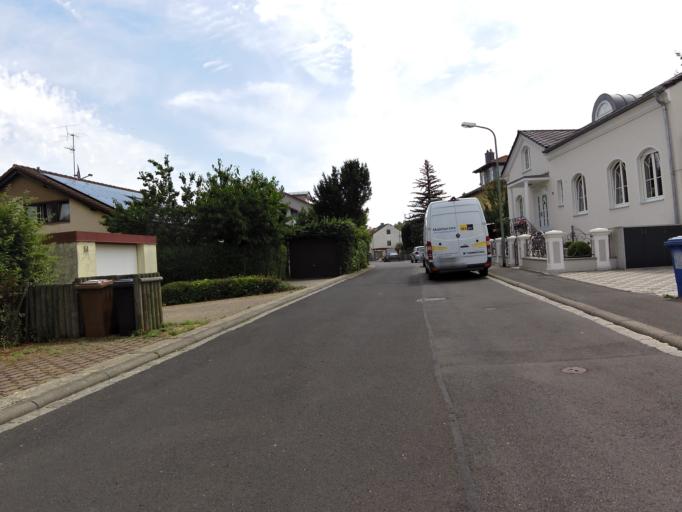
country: DE
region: Bavaria
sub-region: Regierungsbezirk Unterfranken
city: Randersacker
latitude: 49.7603
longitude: 9.9514
